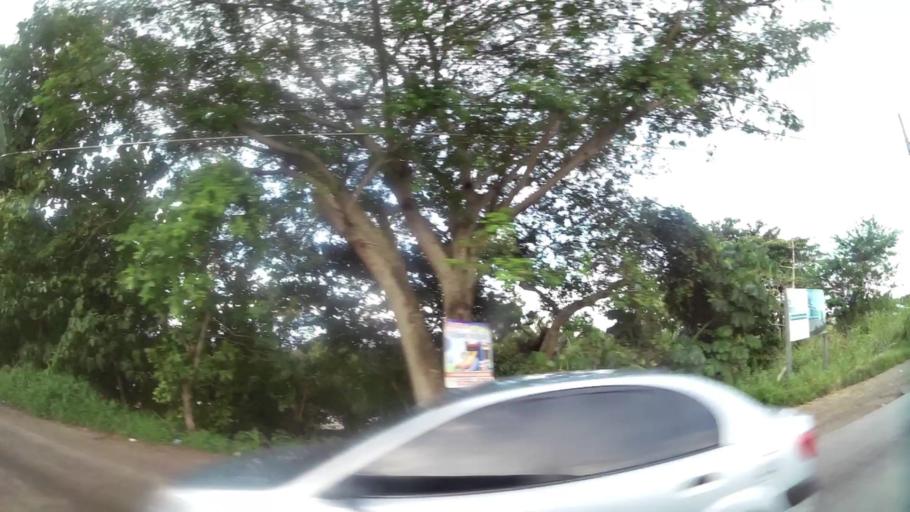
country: PA
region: Panama
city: La Chorrera
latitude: 8.8691
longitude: -79.7706
